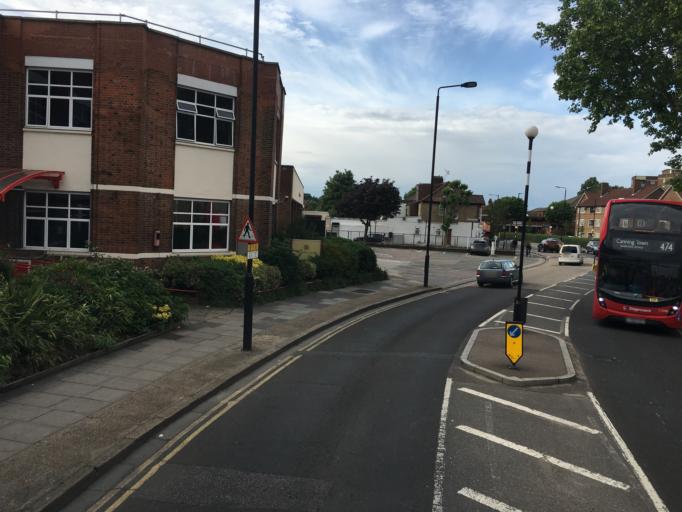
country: GB
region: England
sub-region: Greater London
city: East Ham
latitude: 51.5232
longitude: 0.0573
